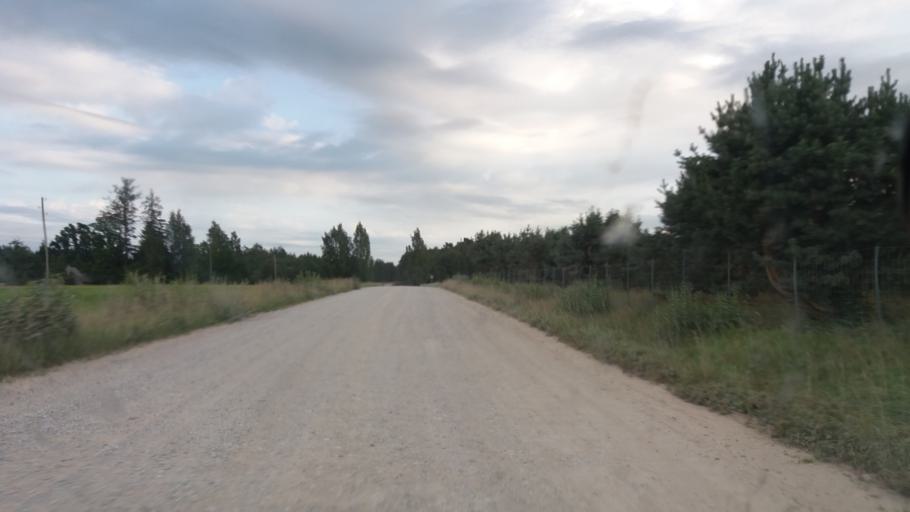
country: LV
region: Talsu Rajons
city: Sabile
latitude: 57.0243
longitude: 22.5861
